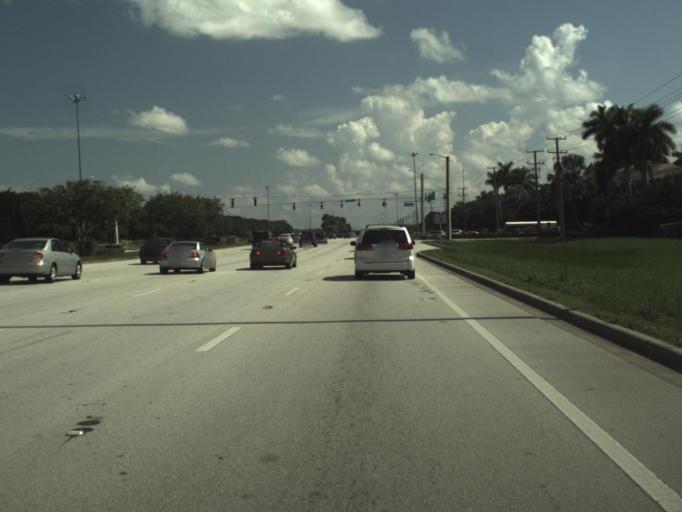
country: US
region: Florida
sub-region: Palm Beach County
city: Wellington
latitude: 26.6450
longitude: -80.2039
